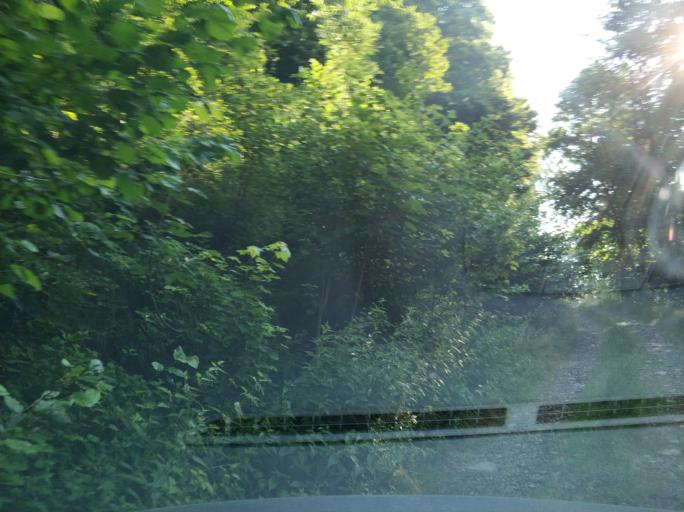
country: IT
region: Piedmont
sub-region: Provincia di Torino
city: Ceres
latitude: 45.3082
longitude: 7.3574
